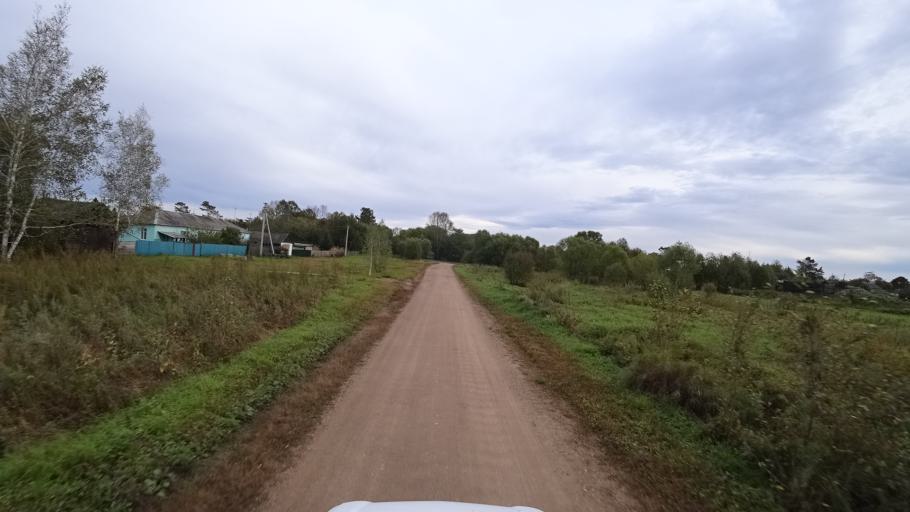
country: RU
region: Amur
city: Arkhara
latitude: 49.4358
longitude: 130.2646
